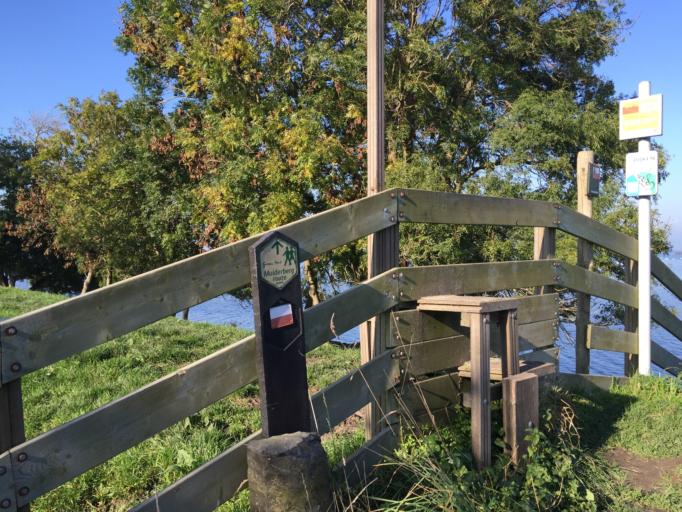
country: NL
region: North Holland
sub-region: Gemeente Weesp
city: Weesp
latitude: 52.3387
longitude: 5.0892
